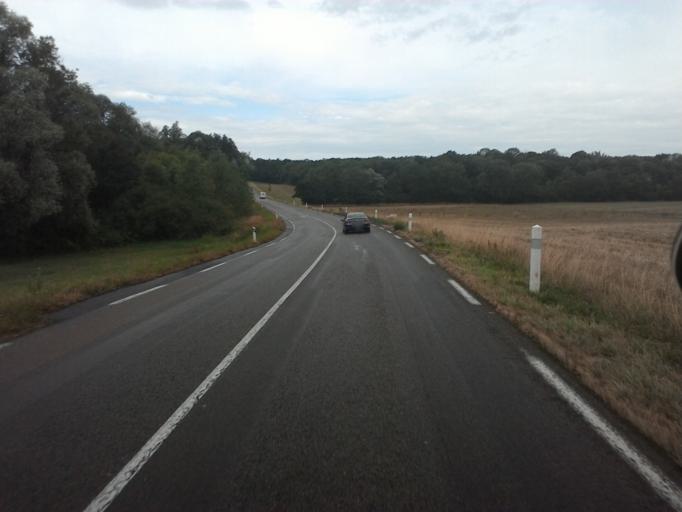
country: FR
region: Franche-Comte
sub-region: Departement du Jura
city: Poligny
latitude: 46.8455
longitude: 5.6339
